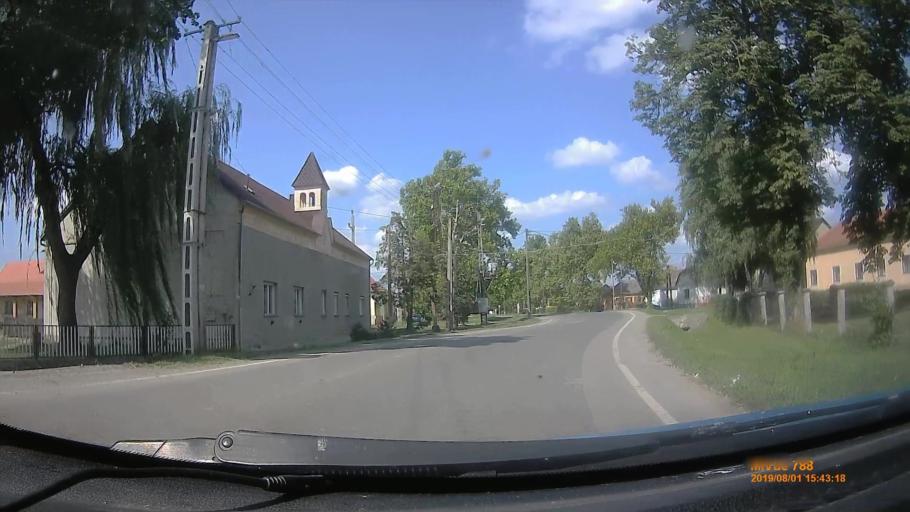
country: HU
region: Baranya
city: Szentlorinc
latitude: 45.9989
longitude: 17.9692
